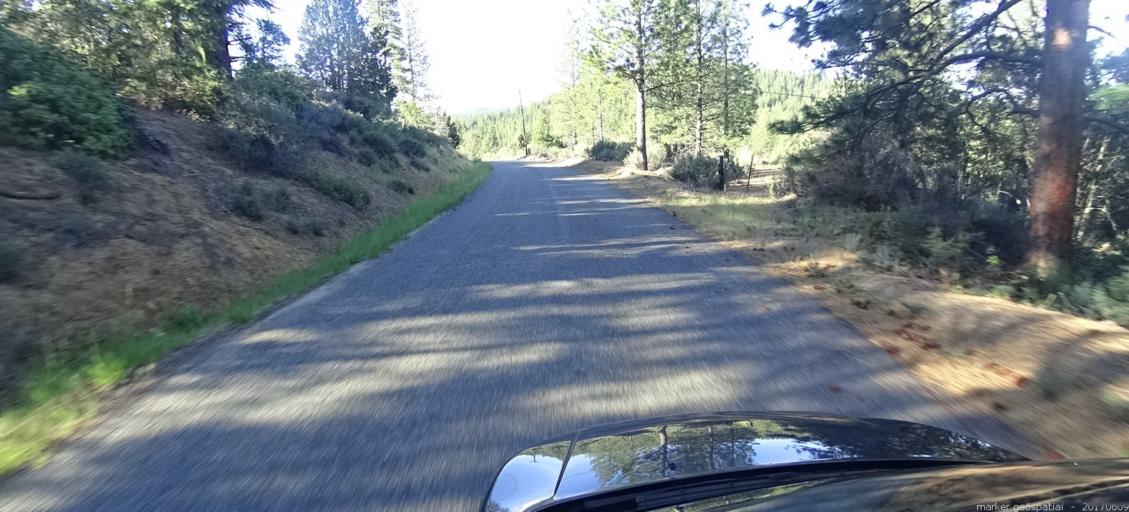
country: US
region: California
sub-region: Siskiyou County
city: Weed
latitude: 41.3859
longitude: -122.6733
